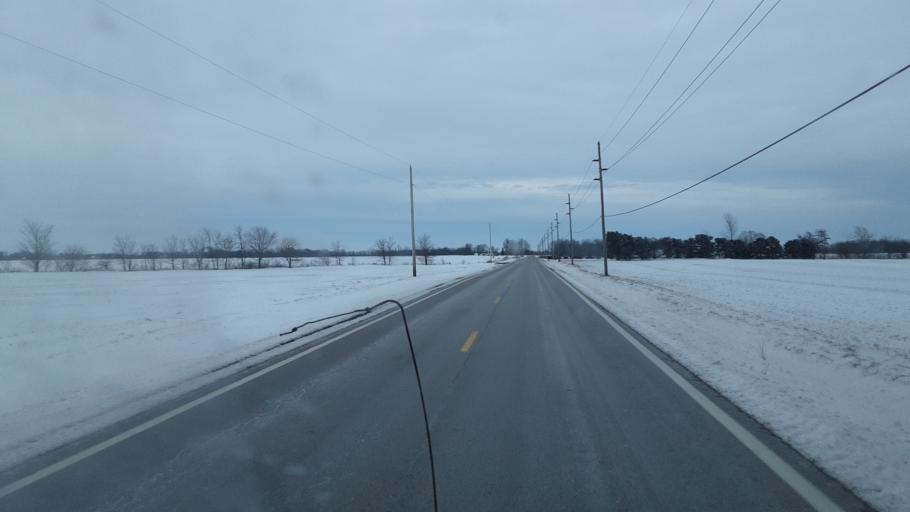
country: US
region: Ohio
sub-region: Madison County
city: Mount Sterling
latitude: 39.6849
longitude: -83.2064
